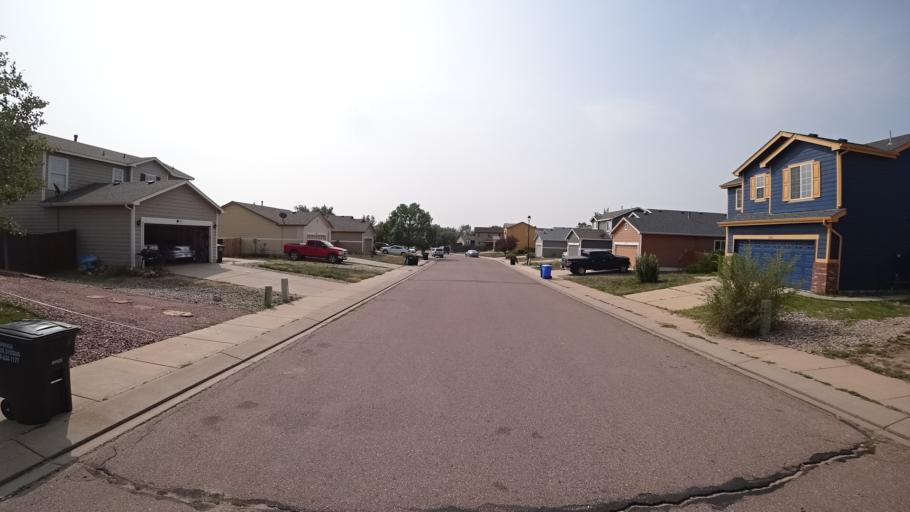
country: US
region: Colorado
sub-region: El Paso County
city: Stratmoor
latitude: 38.7978
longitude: -104.7624
